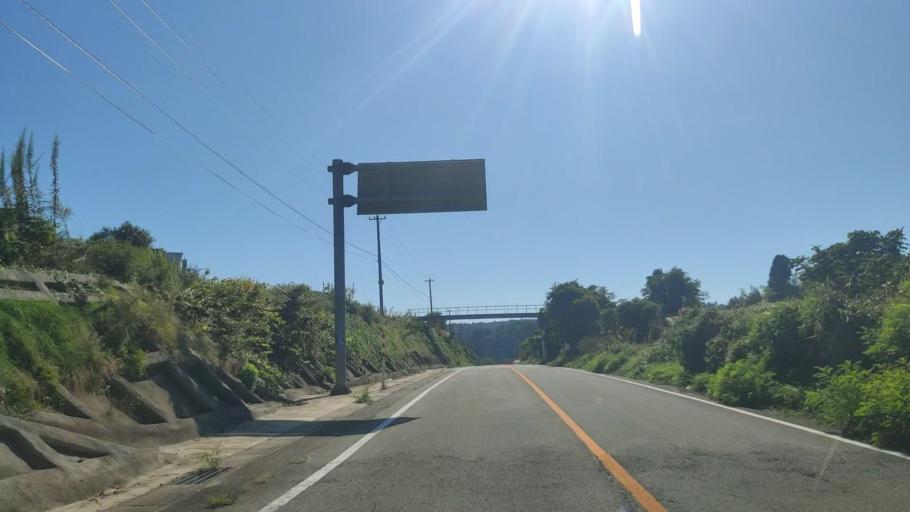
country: JP
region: Ishikawa
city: Nanao
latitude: 37.2670
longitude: 137.0935
